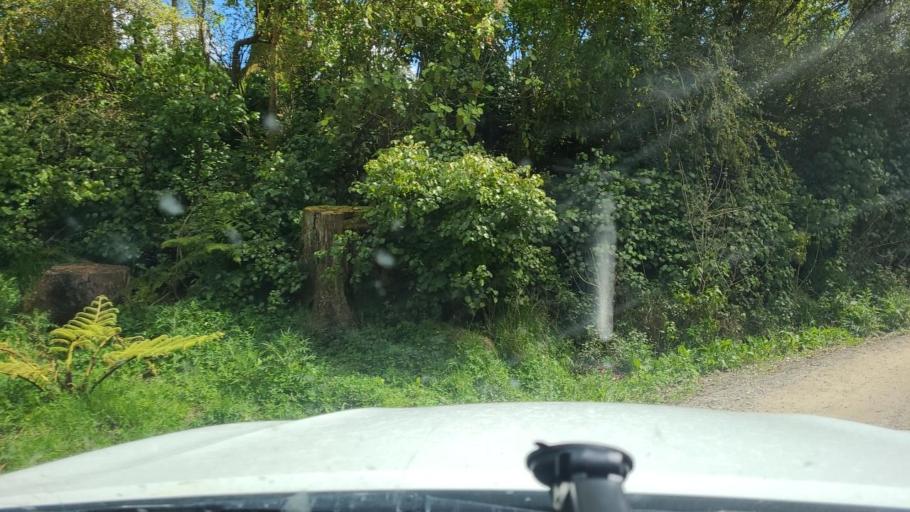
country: NZ
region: Gisborne
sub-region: Gisborne District
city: Gisborne
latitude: -38.7863
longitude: 177.7750
